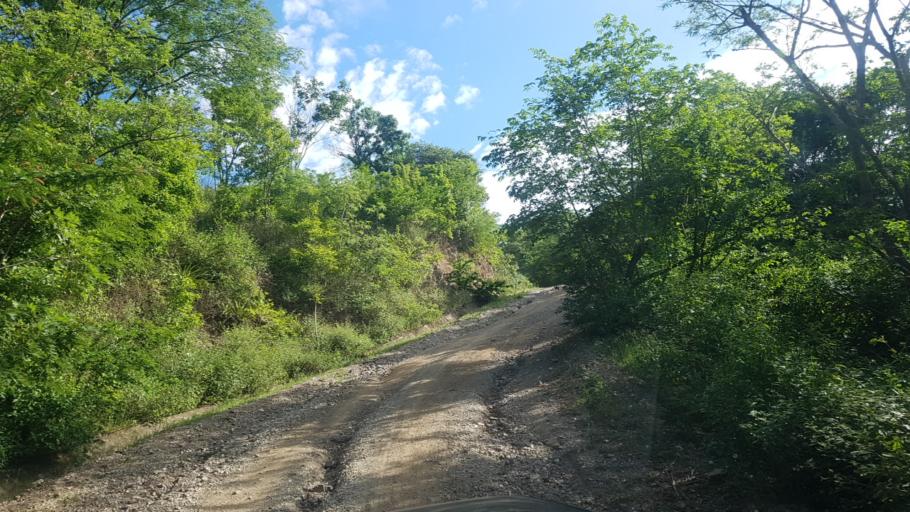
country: NI
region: Nueva Segovia
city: Ocotal
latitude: 13.6073
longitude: -86.4639
